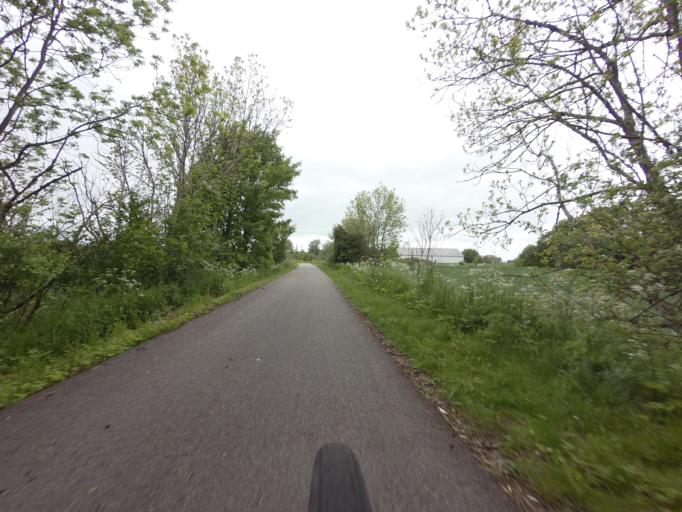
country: DK
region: Zealand
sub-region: Naestved Kommune
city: Fuglebjerg
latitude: 55.2881
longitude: 11.4252
